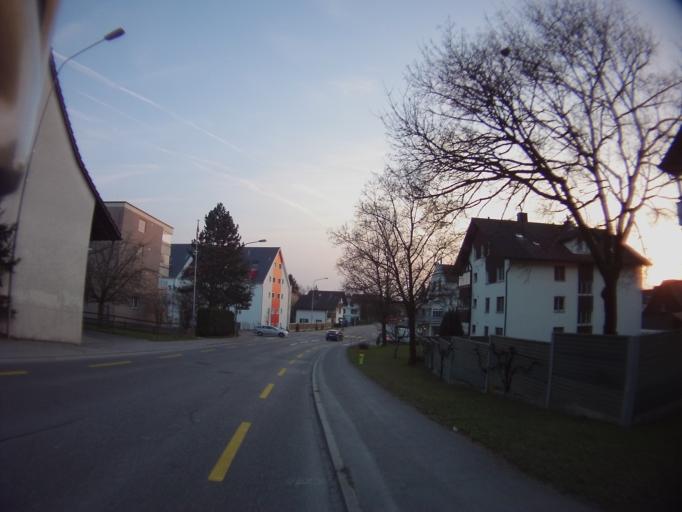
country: CH
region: Zurich
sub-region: Bezirk Affoltern
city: Obfelden / Toussen
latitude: 47.2660
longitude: 8.4332
